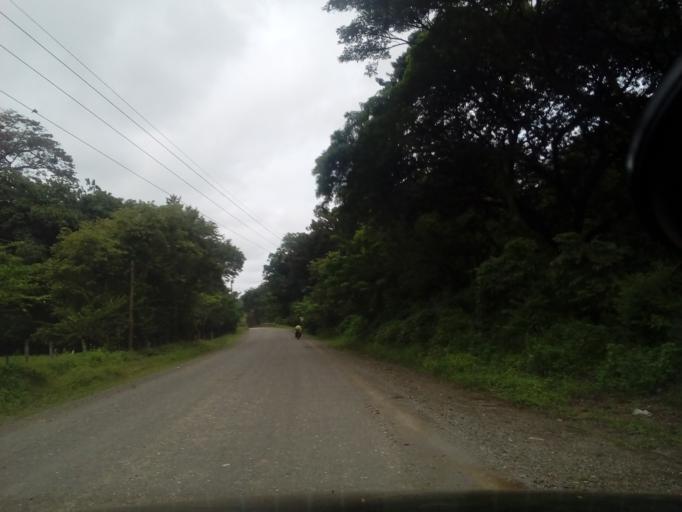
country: CR
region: Guanacaste
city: Samara
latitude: 9.9149
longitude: -85.6275
